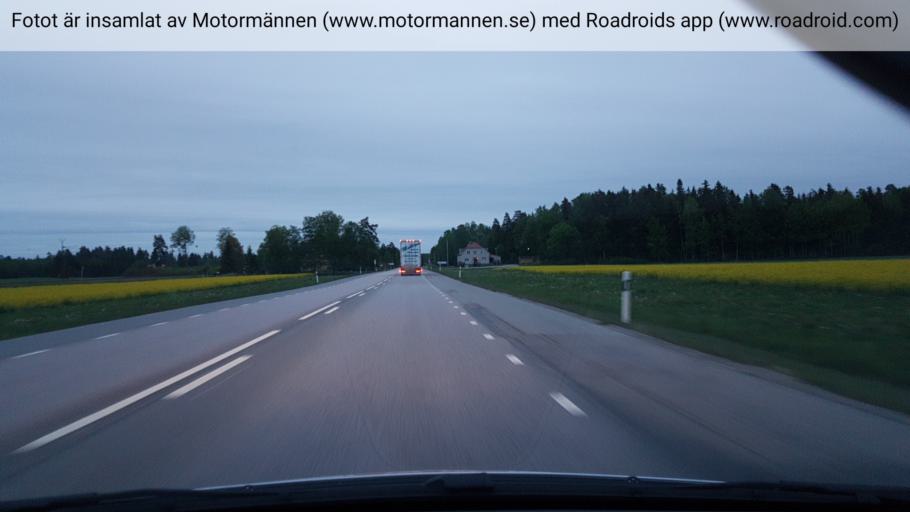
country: SE
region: Uppsala
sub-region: Heby Kommun
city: Heby
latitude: 59.9341
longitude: 16.7343
